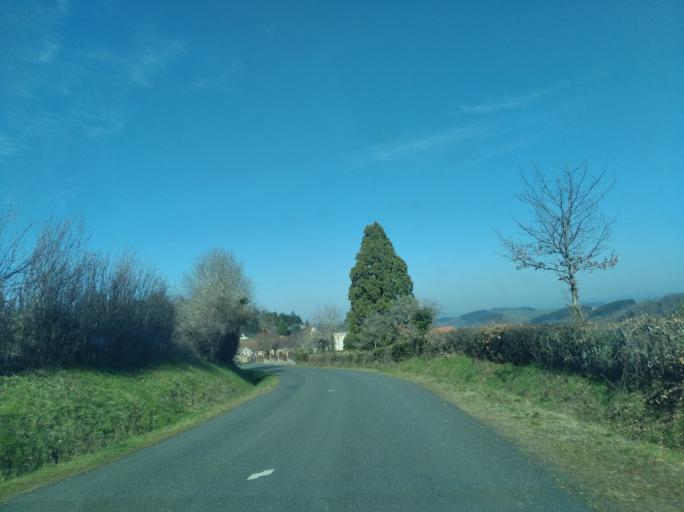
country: FR
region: Auvergne
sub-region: Departement de l'Allier
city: Le Mayet-de-Montagne
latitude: 46.1065
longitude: 3.6892
